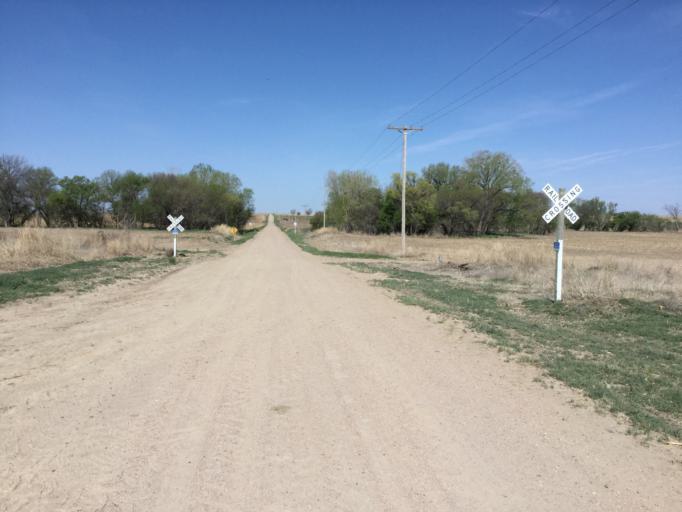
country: US
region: Kansas
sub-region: Decatur County
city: Oberlin
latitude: 39.9730
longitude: -100.5734
